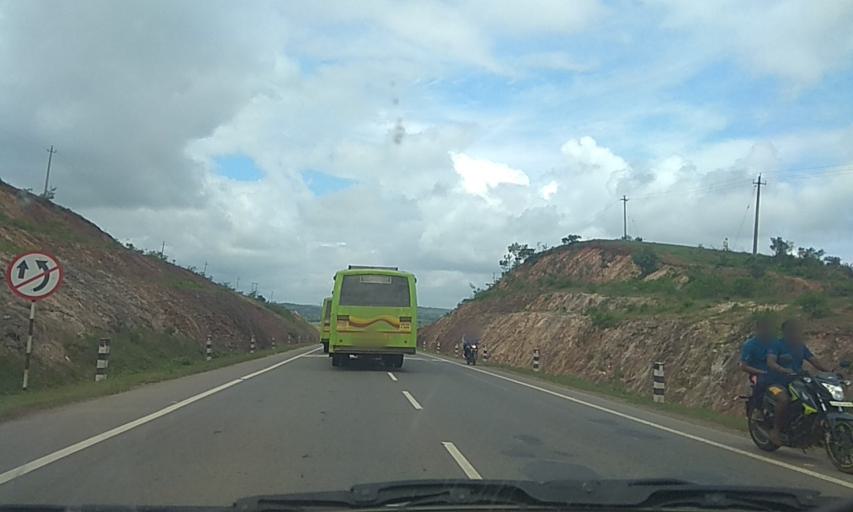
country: IN
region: Karnataka
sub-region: Dharwad
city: Hubli
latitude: 15.4015
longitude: 74.9970
